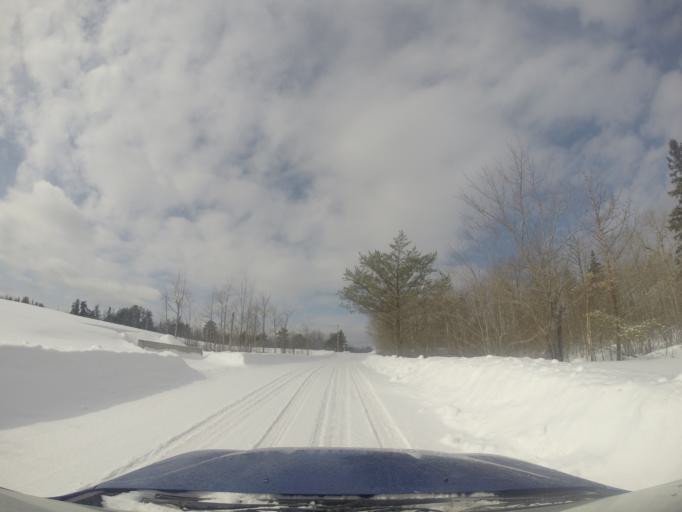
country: CA
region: Ontario
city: Greater Sudbury
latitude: 46.1048
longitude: -80.6743
